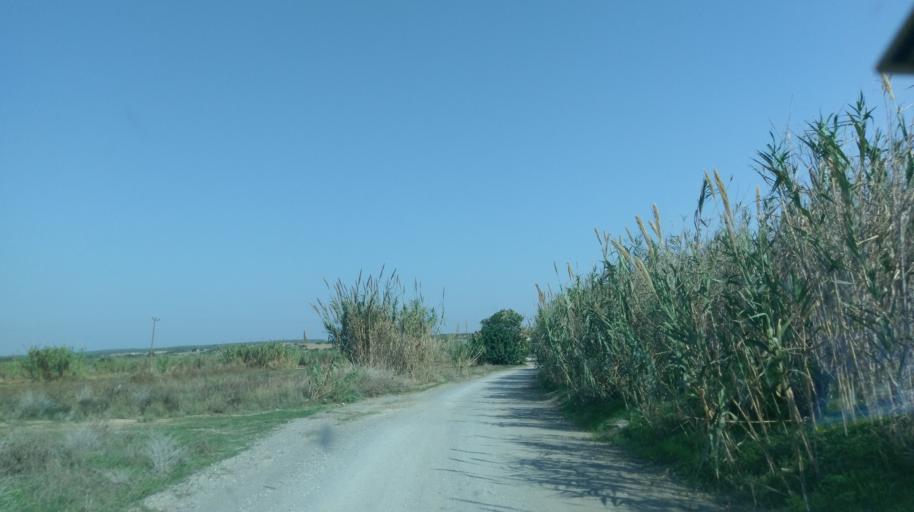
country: CY
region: Lefkosia
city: Morfou
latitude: 35.2920
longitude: 32.9510
